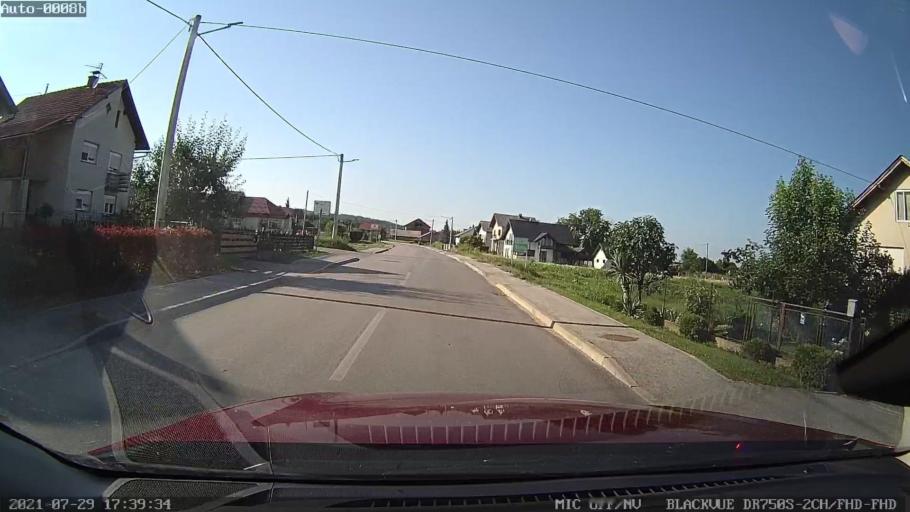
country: HR
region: Varazdinska
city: Vinica
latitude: 46.3163
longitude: 16.1582
